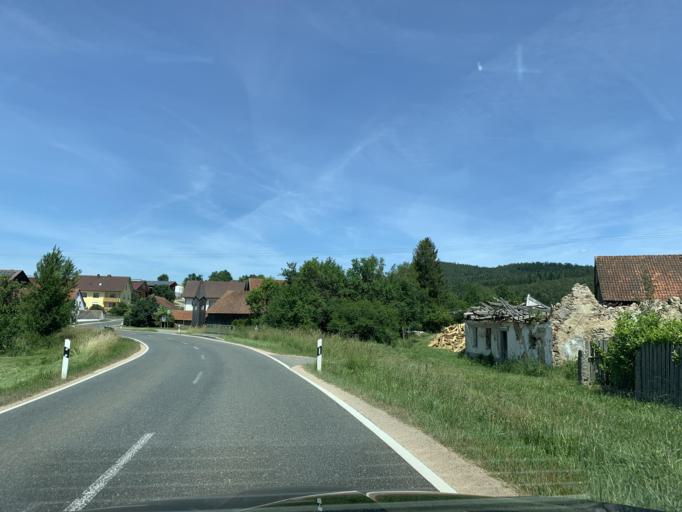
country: DE
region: Bavaria
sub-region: Upper Palatinate
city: Schwarzhofen
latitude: 49.3866
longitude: 12.3537
